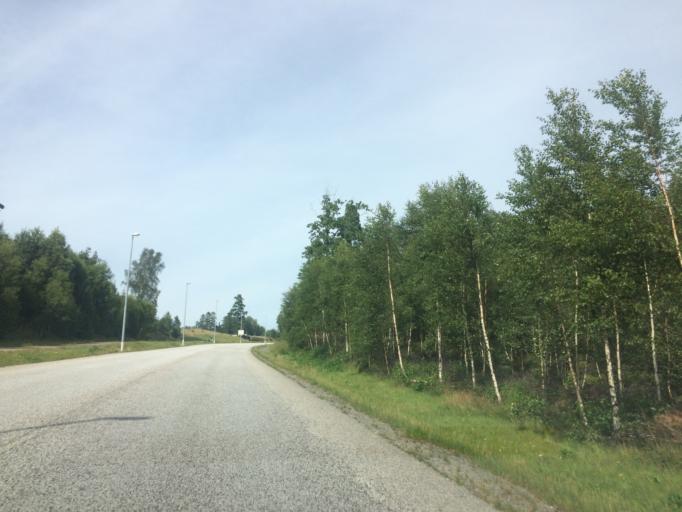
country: SE
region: Vaestra Goetaland
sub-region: Partille Kommun
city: Ojersjo
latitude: 57.6807
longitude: 12.0952
